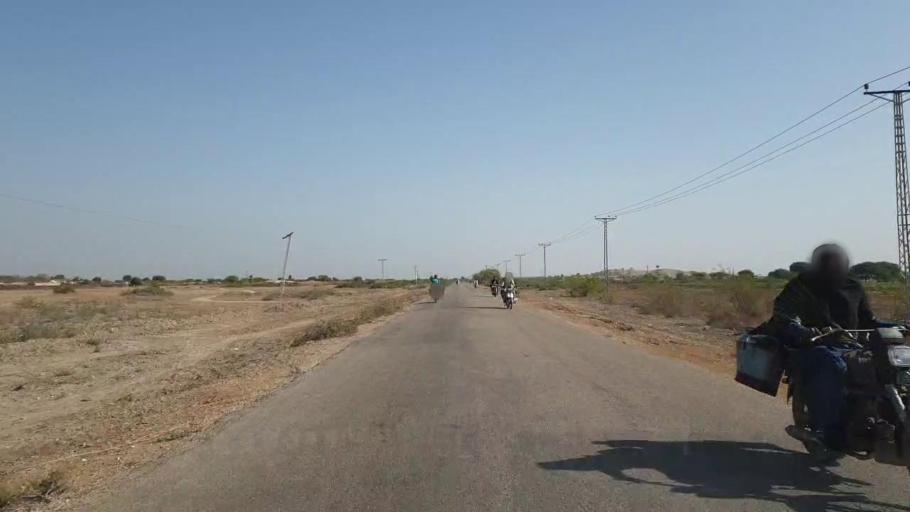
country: PK
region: Sindh
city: Umarkot
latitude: 25.4195
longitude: 69.7348
